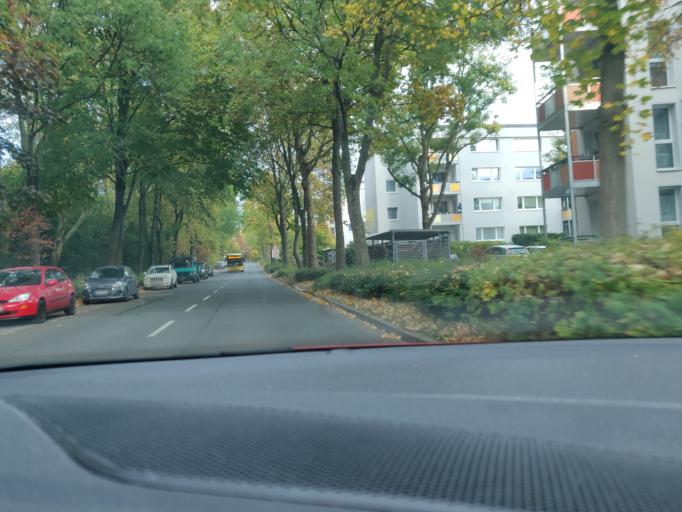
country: DE
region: North Rhine-Westphalia
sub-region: Regierungsbezirk Dusseldorf
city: Velbert
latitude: 51.3409
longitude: 7.0144
